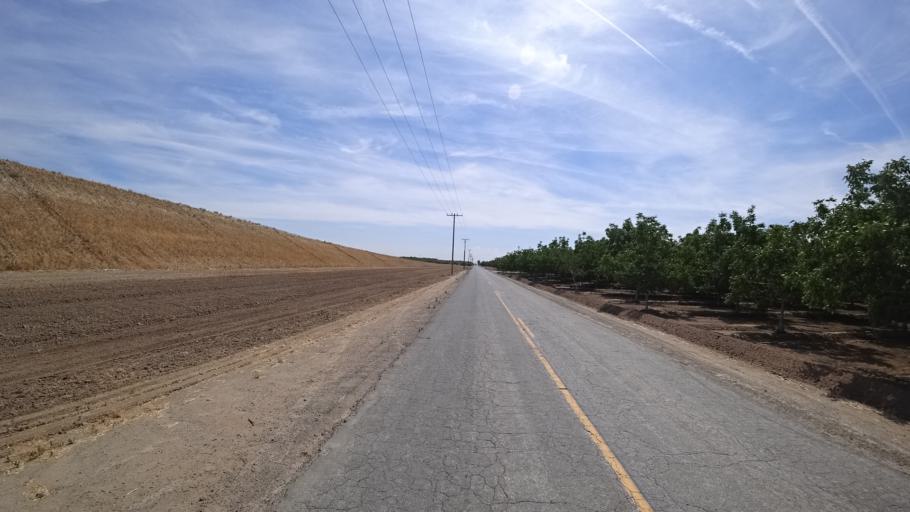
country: US
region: California
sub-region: Kings County
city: Hanford
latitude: 36.3572
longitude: -119.5911
